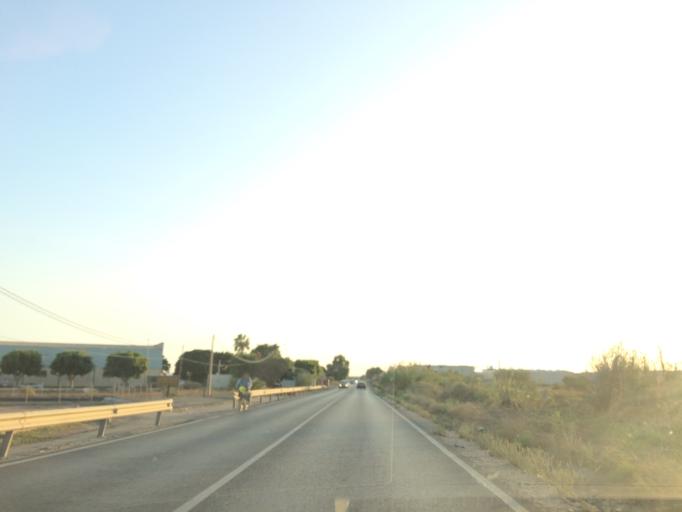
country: ES
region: Andalusia
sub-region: Provincia de Almeria
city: Nijar
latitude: 36.9301
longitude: -2.1405
